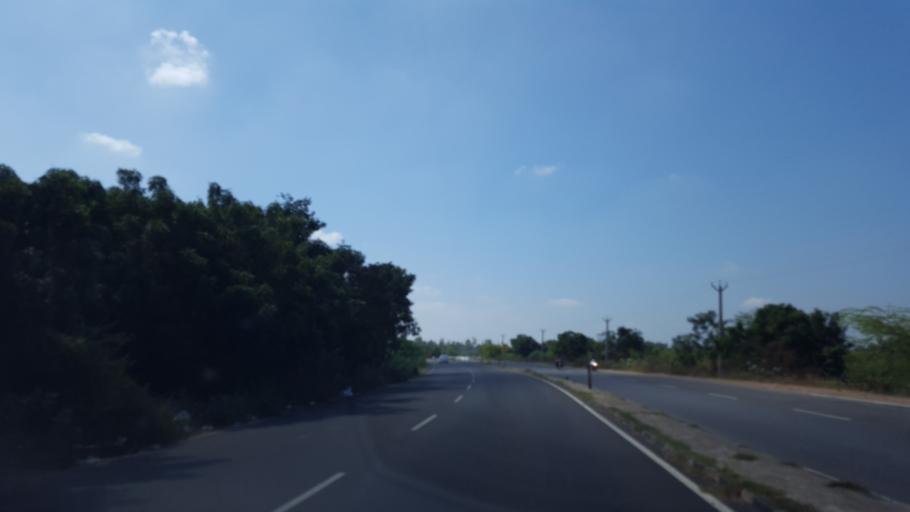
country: IN
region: Tamil Nadu
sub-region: Kancheepuram
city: Mamallapuram
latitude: 12.7066
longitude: 80.1846
